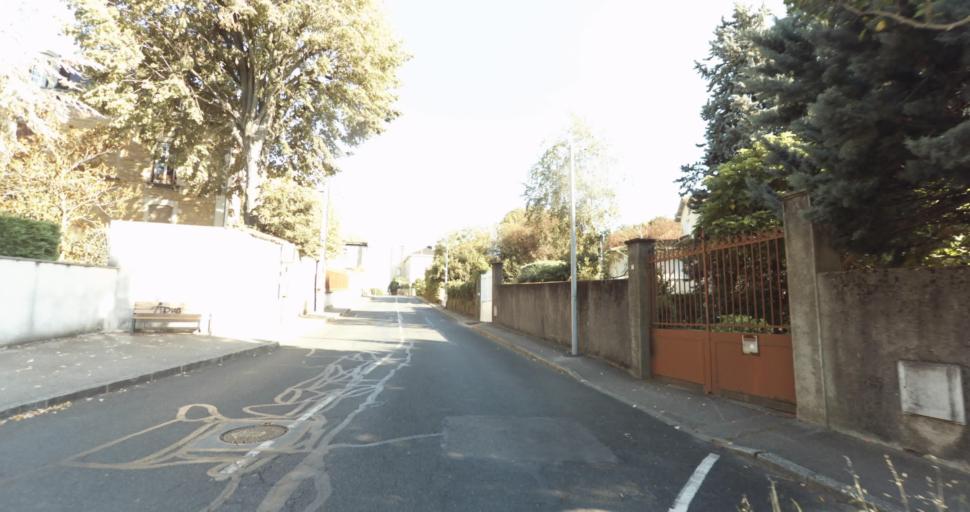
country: FR
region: Rhone-Alpes
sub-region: Departement du Rhone
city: Neuville-sur-Saone
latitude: 45.8825
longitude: 4.8371
